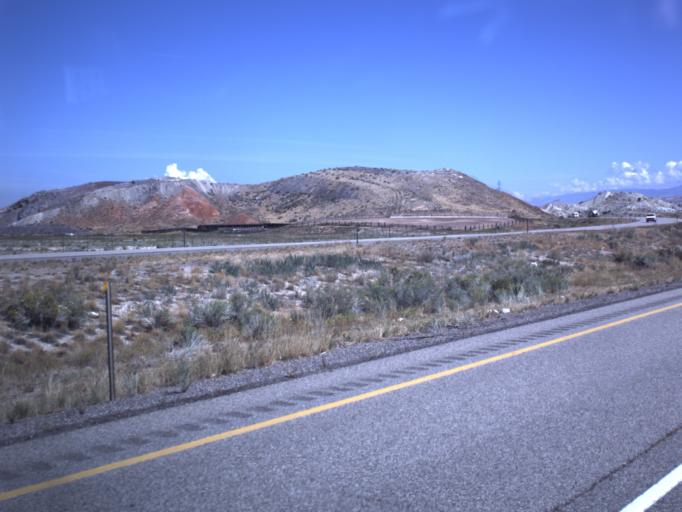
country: US
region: Utah
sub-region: Sevier County
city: Aurora
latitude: 38.8888
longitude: -111.9103
